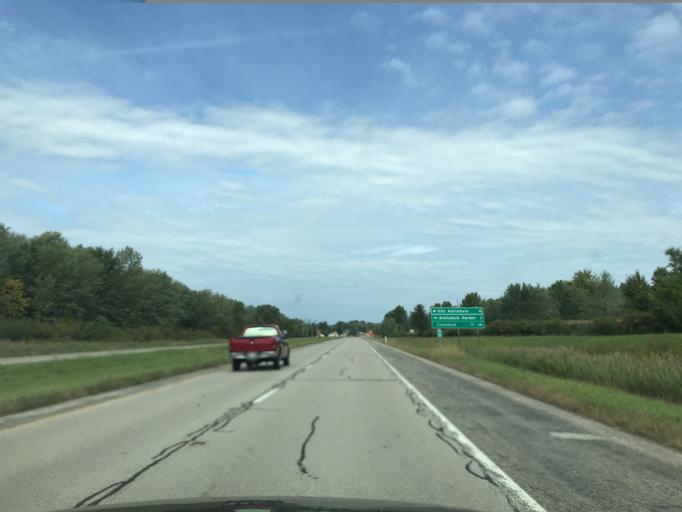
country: US
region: Ohio
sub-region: Ashtabula County
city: Edgewood
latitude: 41.8958
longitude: -80.7817
